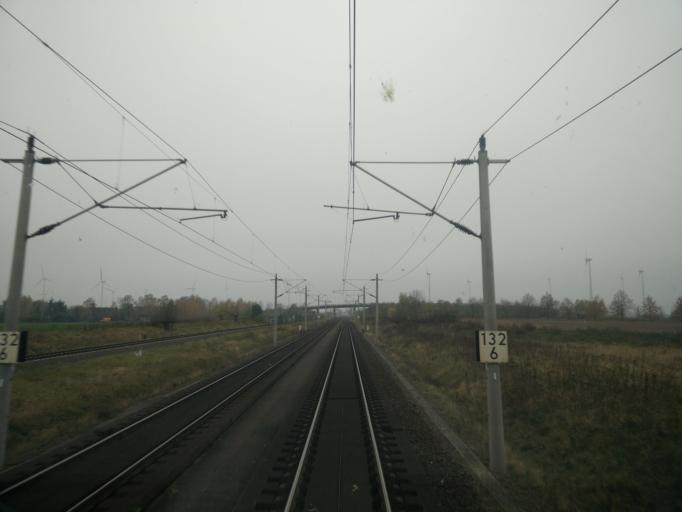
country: DE
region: Brandenburg
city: Wustermark
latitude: 52.5543
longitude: 12.9077
